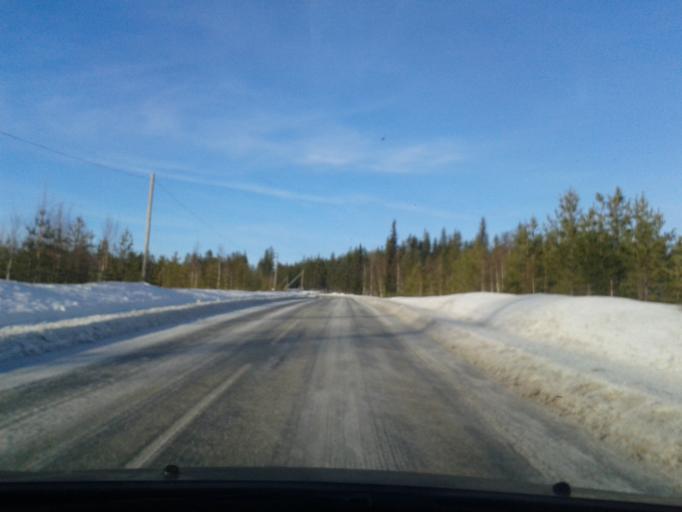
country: SE
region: Vaesternorrland
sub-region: OErnskoeldsviks Kommun
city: Bredbyn
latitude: 63.7280
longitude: 17.7475
